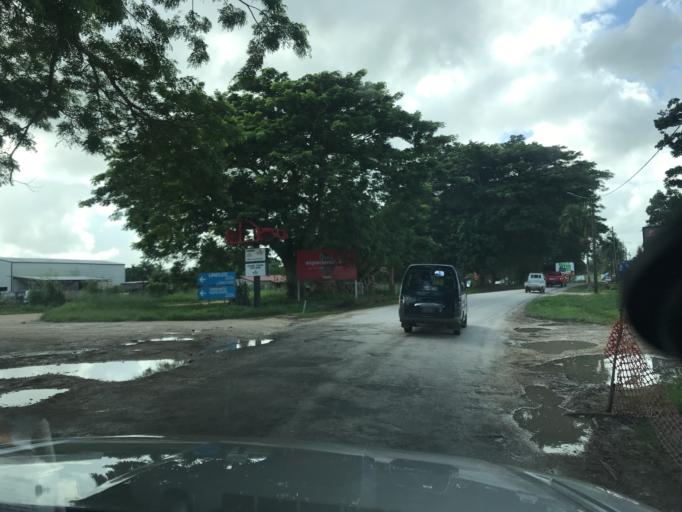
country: VU
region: Shefa
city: Port-Vila
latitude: -17.7057
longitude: 168.3157
